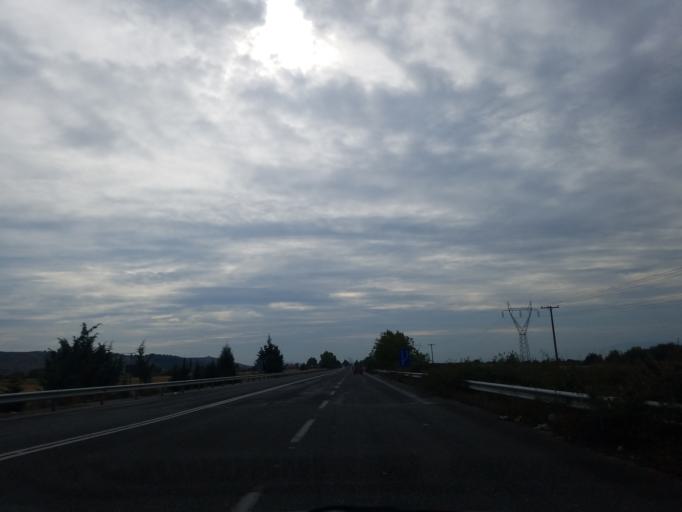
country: GR
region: Thessaly
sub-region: Trikala
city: Vasiliki
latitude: 39.6606
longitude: 21.6747
